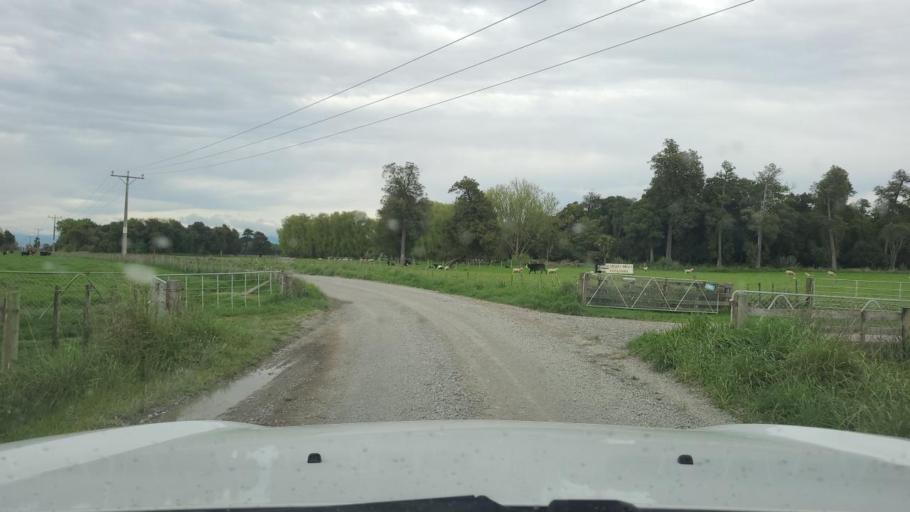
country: NZ
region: Wellington
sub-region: South Wairarapa District
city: Waipawa
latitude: -41.2283
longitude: 175.4139
